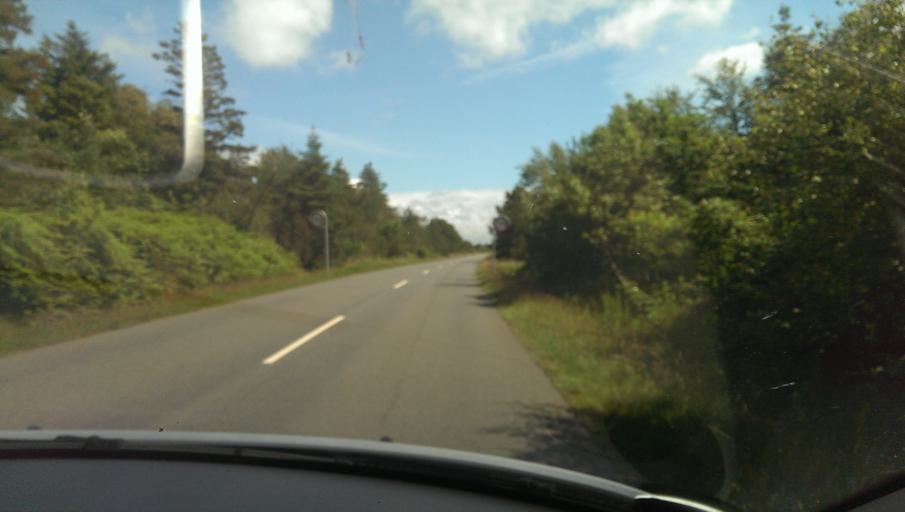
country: DK
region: Central Jutland
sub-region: Ringkobing-Skjern Kommune
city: Ringkobing
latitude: 56.1429
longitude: 8.1436
